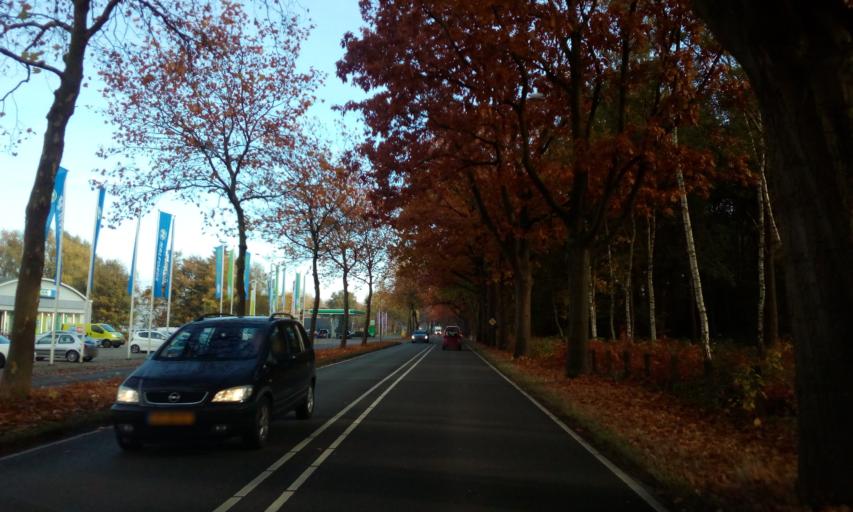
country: NL
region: Gelderland
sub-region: Gemeente Apeldoorn
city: Apeldoorn
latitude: 52.1942
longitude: 5.9388
